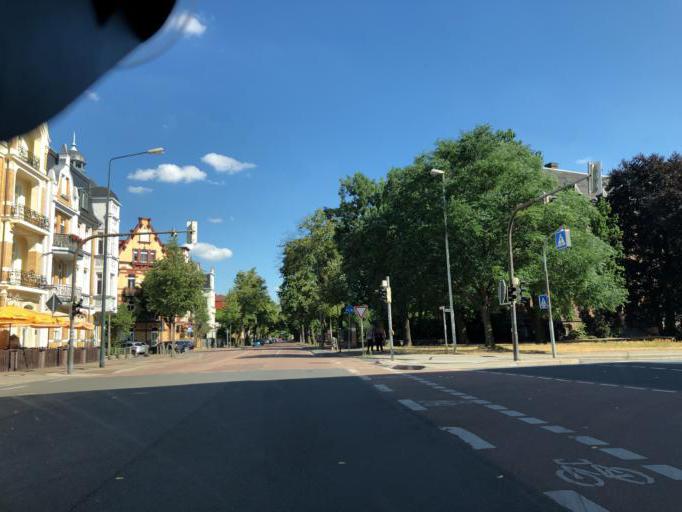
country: DE
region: Saxony-Anhalt
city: Wittenburg
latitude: 51.8689
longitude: 12.6493
